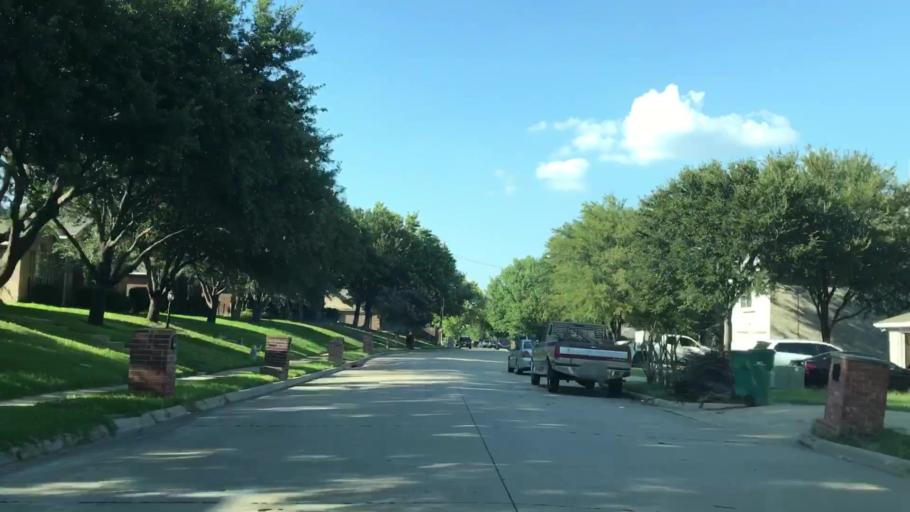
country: US
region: Texas
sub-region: Denton County
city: Lewisville
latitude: 33.0095
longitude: -97.0113
